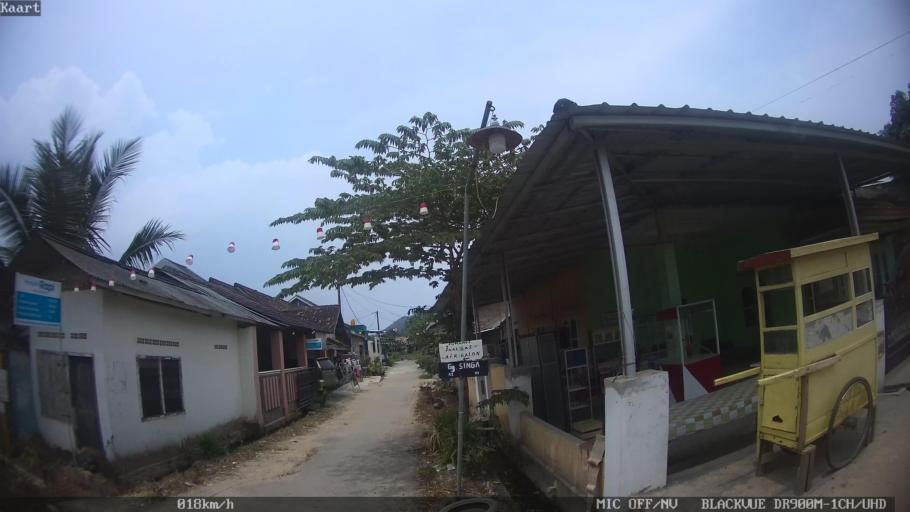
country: ID
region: Lampung
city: Kedaton
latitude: -5.3957
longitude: 105.3203
